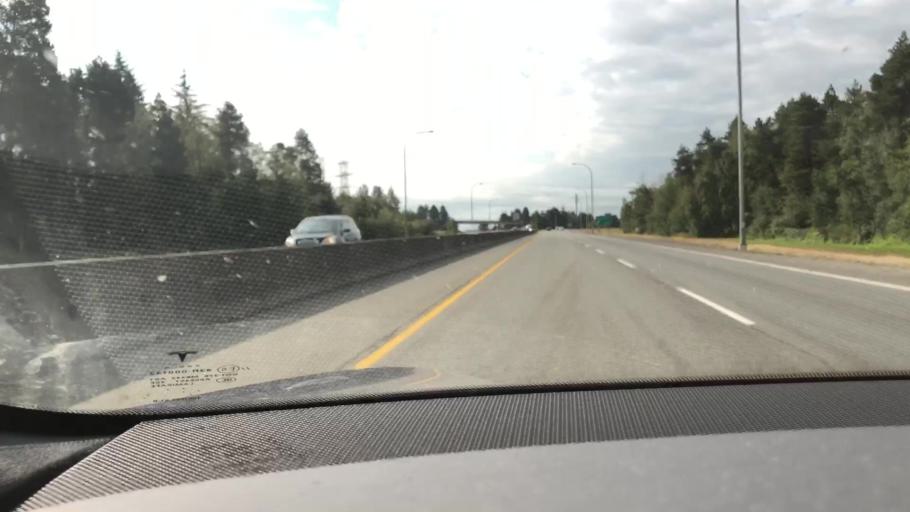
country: CA
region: British Columbia
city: Delta
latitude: 49.1255
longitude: -122.9281
